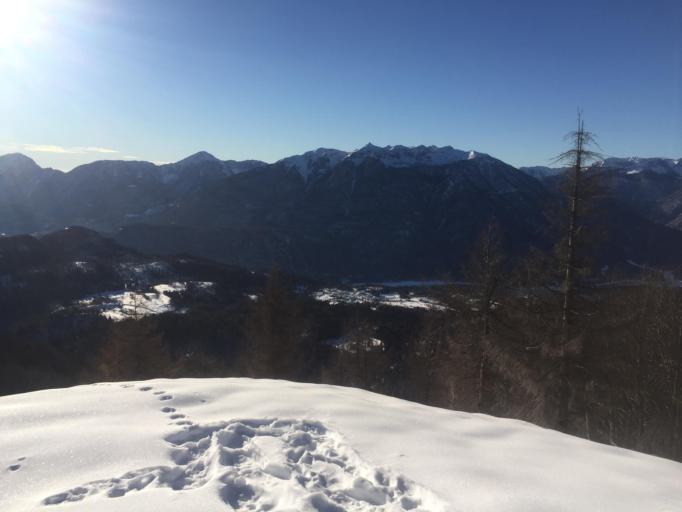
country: IT
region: Friuli Venezia Giulia
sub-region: Provincia di Udine
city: Lauco
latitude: 46.4508
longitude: 12.9373
